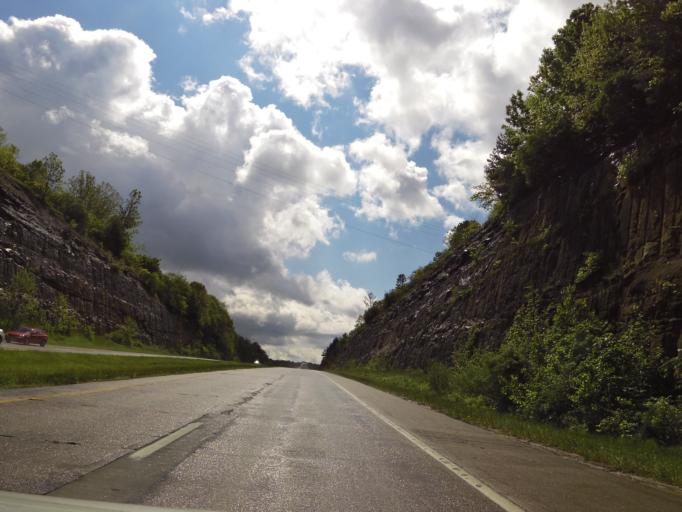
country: US
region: Ohio
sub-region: Athens County
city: Athens
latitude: 39.3543
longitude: -82.0939
